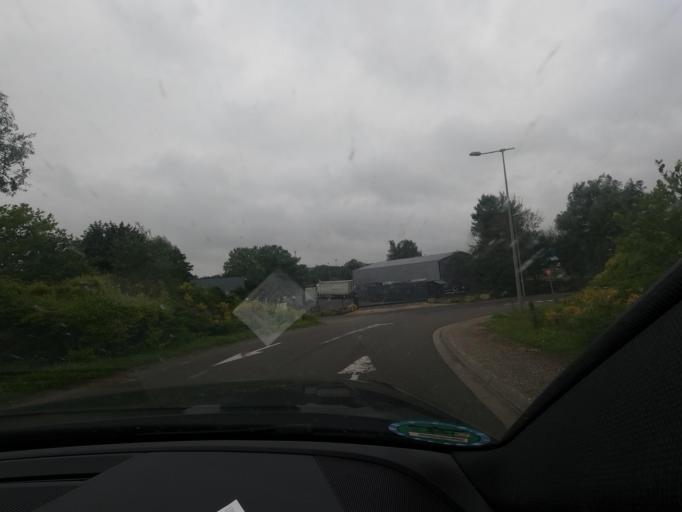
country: FR
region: Picardie
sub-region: Departement de l'Oise
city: Ressons-sur-Matz
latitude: 49.5388
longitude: 2.7320
